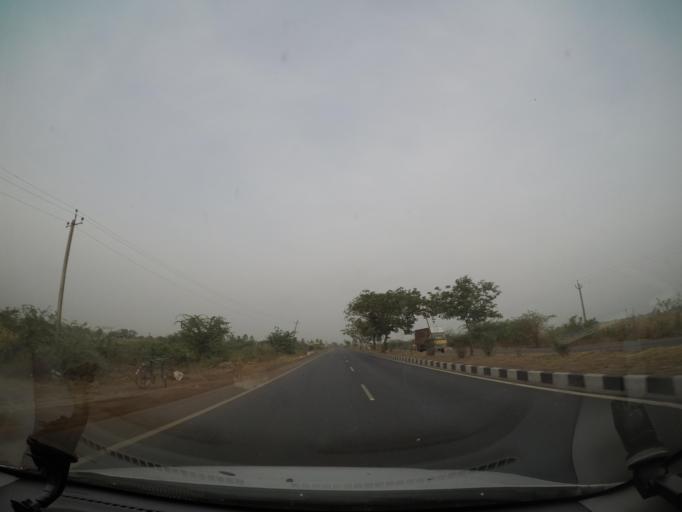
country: IN
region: Andhra Pradesh
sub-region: Krishna
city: Gannavaram
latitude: 16.6290
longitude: 80.9452
